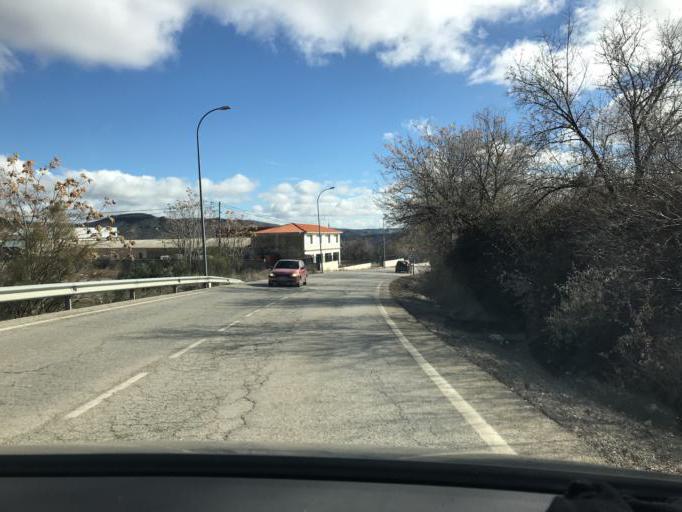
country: ES
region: Andalusia
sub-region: Provincia de Jaen
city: Huelma
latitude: 37.6508
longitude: -3.4485
